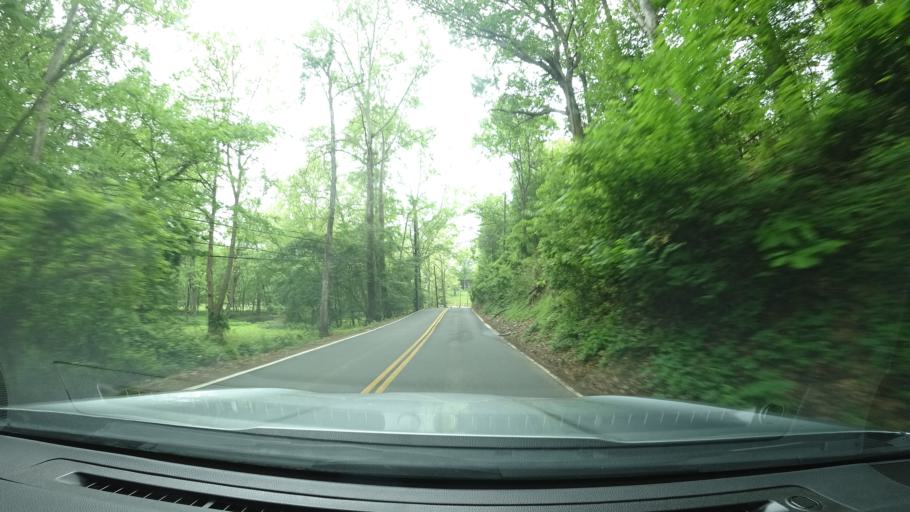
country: US
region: Virginia
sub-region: Fairfax County
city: Oakton
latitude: 38.8795
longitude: -77.3386
